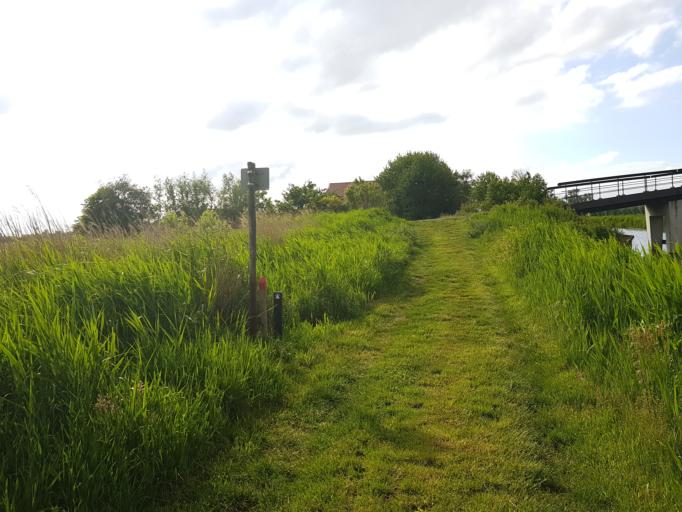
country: NL
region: Friesland
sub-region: Gemeente Smallingerland
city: Oudega
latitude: 53.0926
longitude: 5.9613
